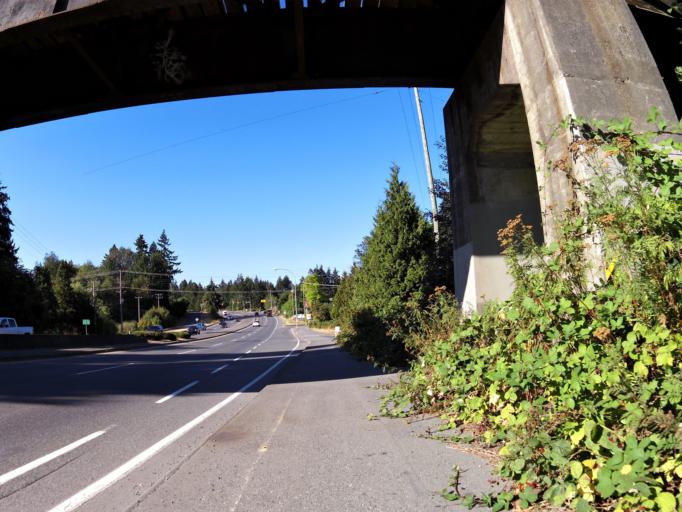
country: CA
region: British Columbia
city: Nanaimo
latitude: 49.1326
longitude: -123.9215
